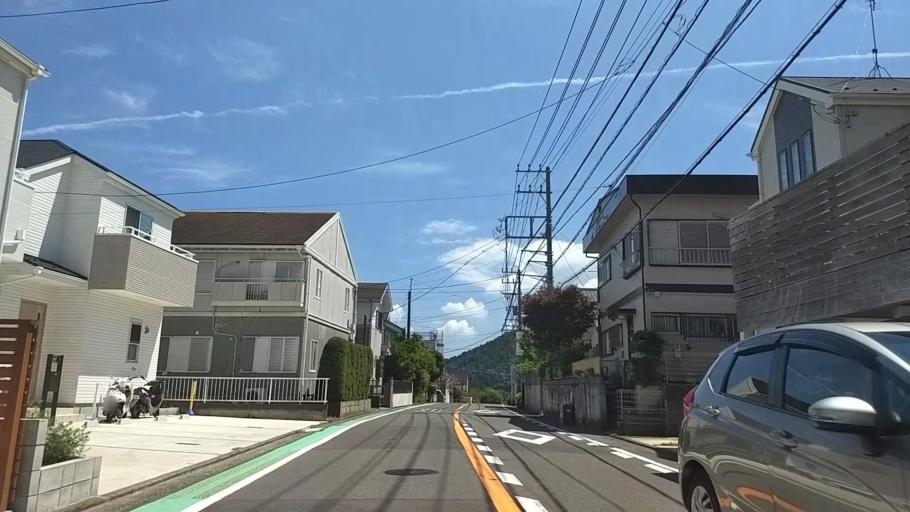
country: JP
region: Kanagawa
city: Zushi
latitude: 35.2906
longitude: 139.5915
